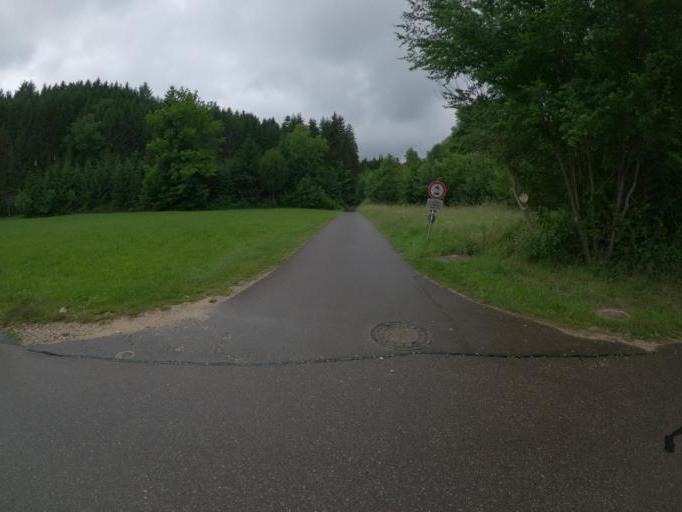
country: DE
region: Baden-Wuerttemberg
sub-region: Regierungsbezirk Stuttgart
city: Bortlingen
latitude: 48.7438
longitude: 9.6202
